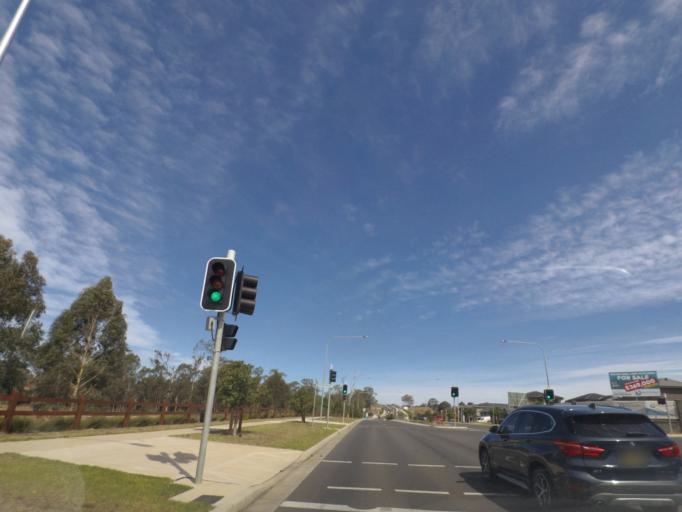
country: AU
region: New South Wales
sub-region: Camden
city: Narellan Vale
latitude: -34.0276
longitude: 150.7856
